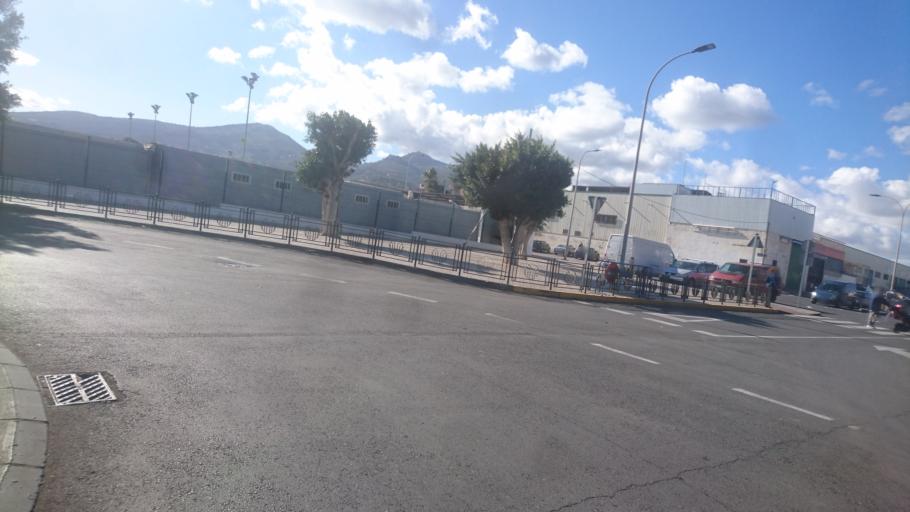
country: ES
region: Melilla
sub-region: Melilla
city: Melilla
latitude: 35.2717
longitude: -2.9401
